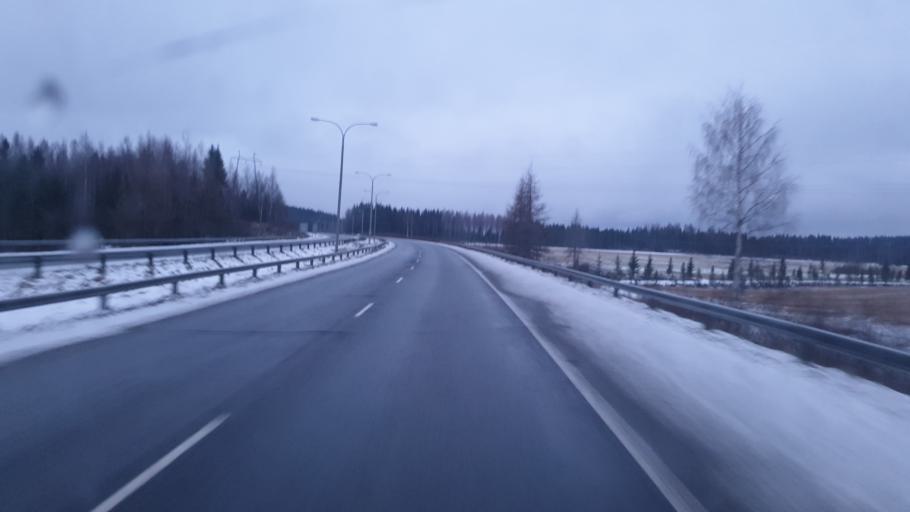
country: FI
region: Northern Savo
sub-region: Kuopio
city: Siilinjaervi
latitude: 63.0487
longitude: 27.6646
